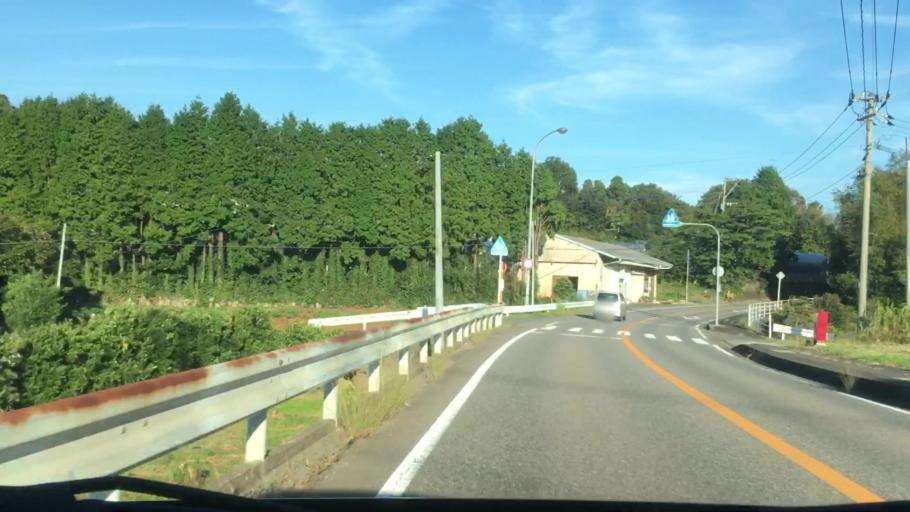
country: JP
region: Nagasaki
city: Sasebo
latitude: 33.0454
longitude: 129.6991
